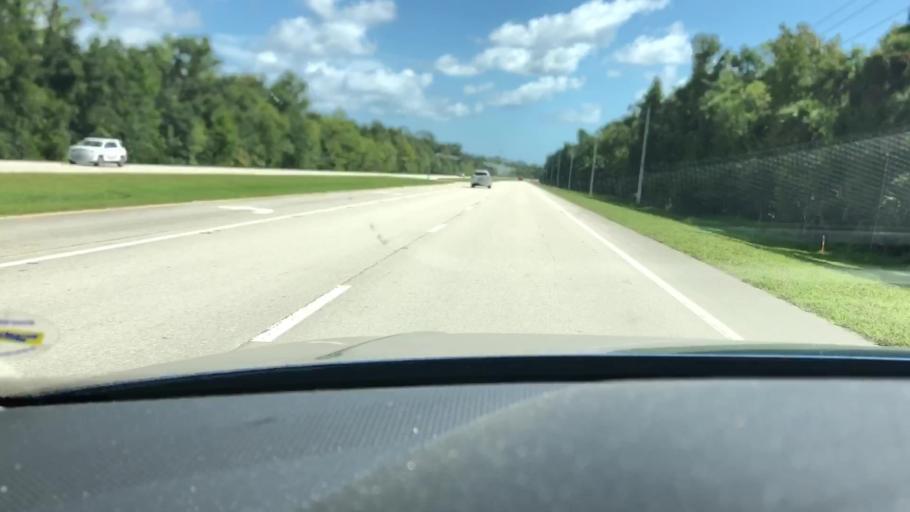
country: US
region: Florida
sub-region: Volusia County
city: Edgewater
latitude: 28.9575
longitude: -80.9307
